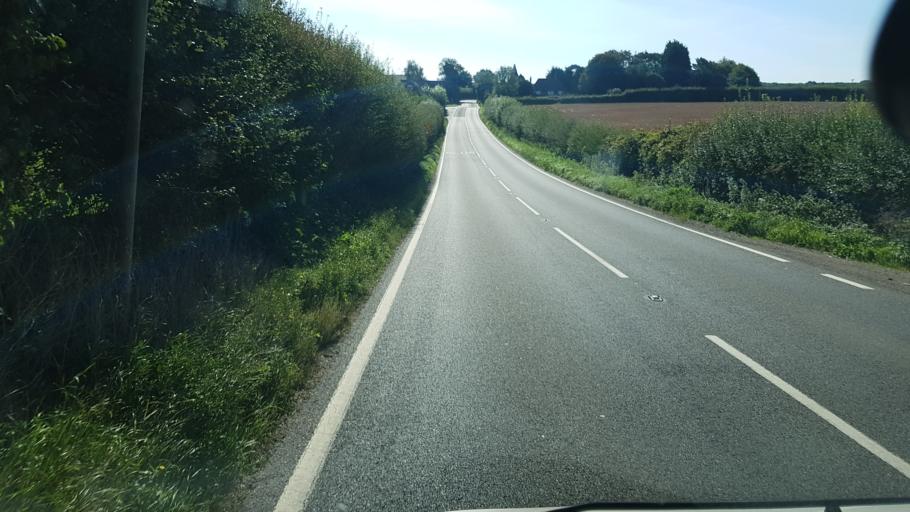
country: GB
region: England
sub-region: Kent
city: Borough Green
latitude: 51.2900
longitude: 0.3491
